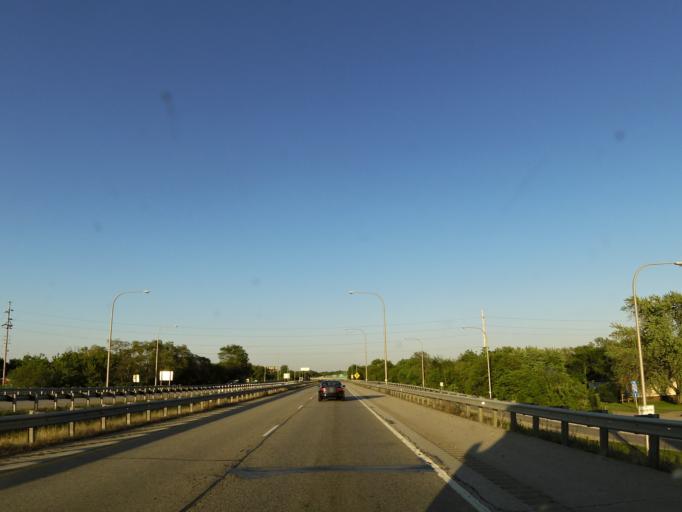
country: US
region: Illinois
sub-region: Vermilion County
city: Tilton
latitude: 40.1048
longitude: -87.6483
